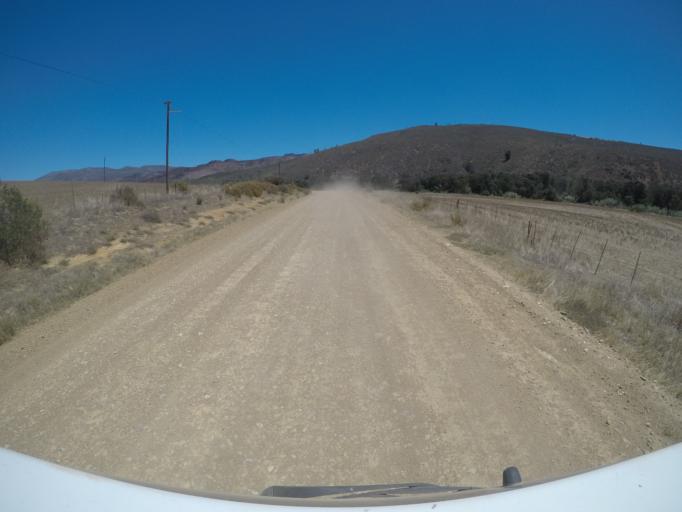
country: ZA
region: Western Cape
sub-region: Overberg District Municipality
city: Caledon
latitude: -34.1481
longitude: 19.2439
